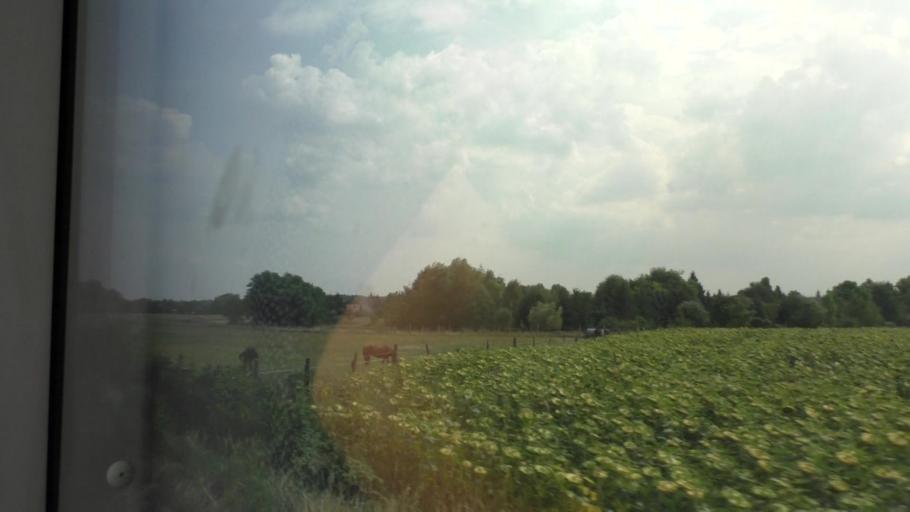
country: DE
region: Brandenburg
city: Tauche
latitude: 52.1750
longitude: 14.1986
